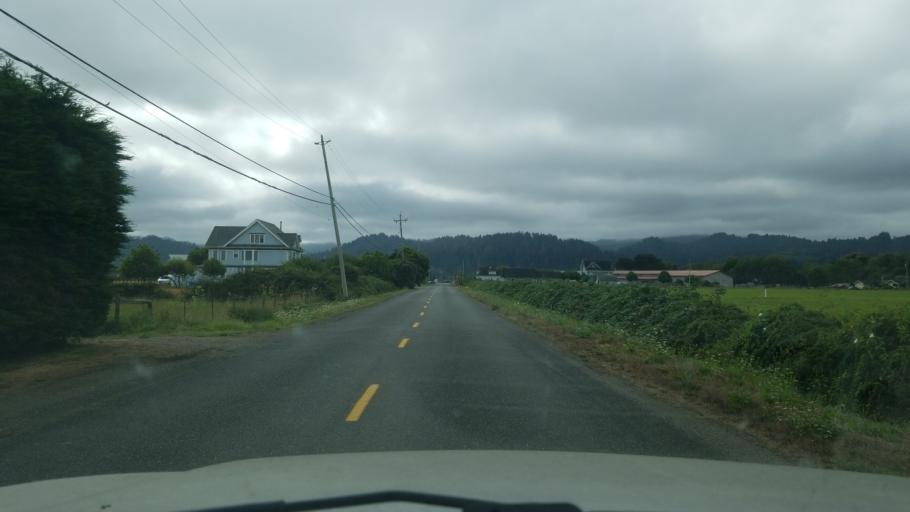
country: US
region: California
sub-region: Humboldt County
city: Ferndale
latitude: 40.5929
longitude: -124.2553
